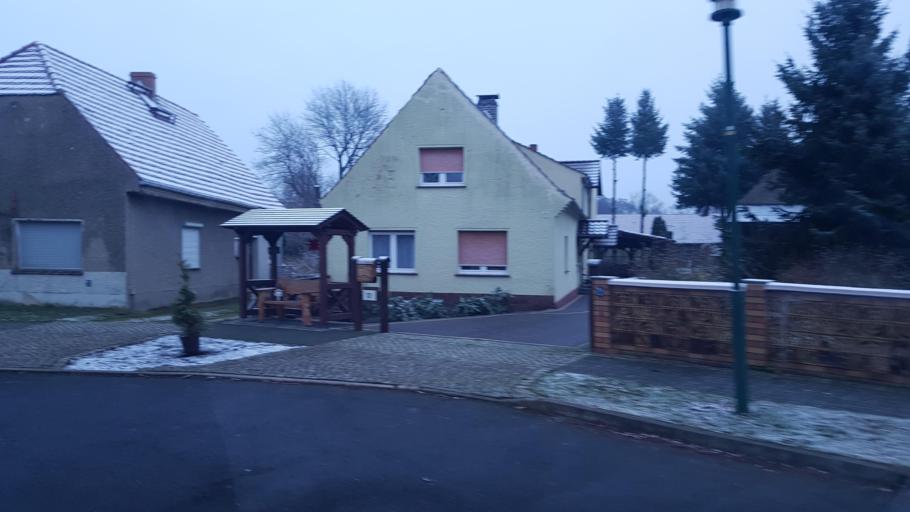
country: DE
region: Brandenburg
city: Kasel-Golzig
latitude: 51.9361
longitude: 13.7864
